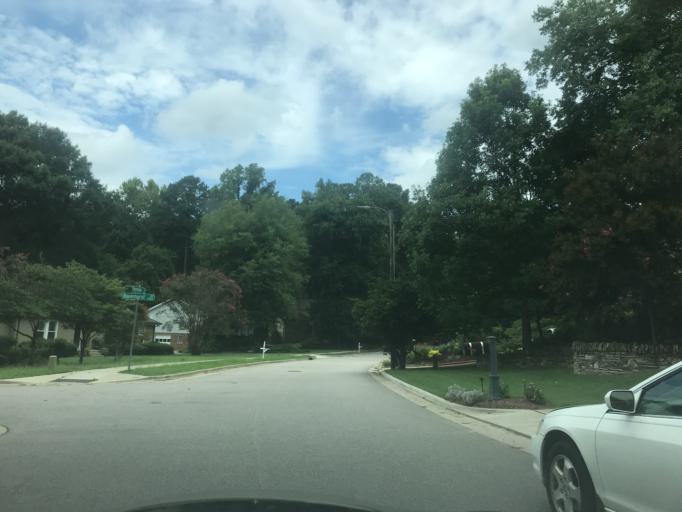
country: US
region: North Carolina
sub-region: Wake County
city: West Raleigh
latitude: 35.8877
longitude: -78.6149
